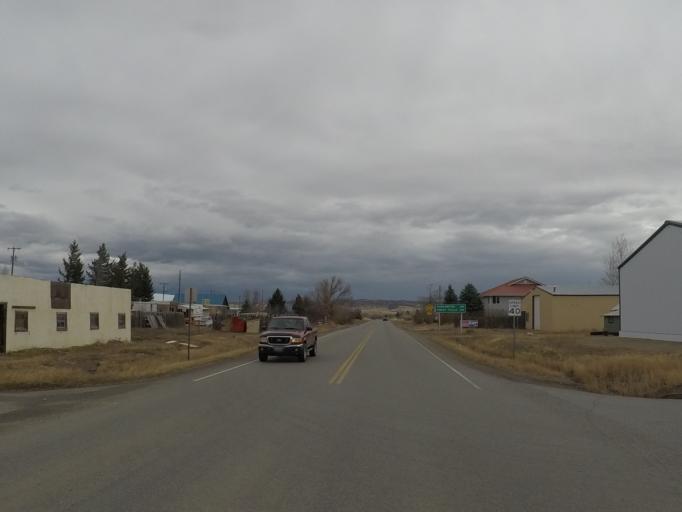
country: US
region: Montana
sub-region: Sweet Grass County
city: Big Timber
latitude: 45.8396
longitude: -109.9475
